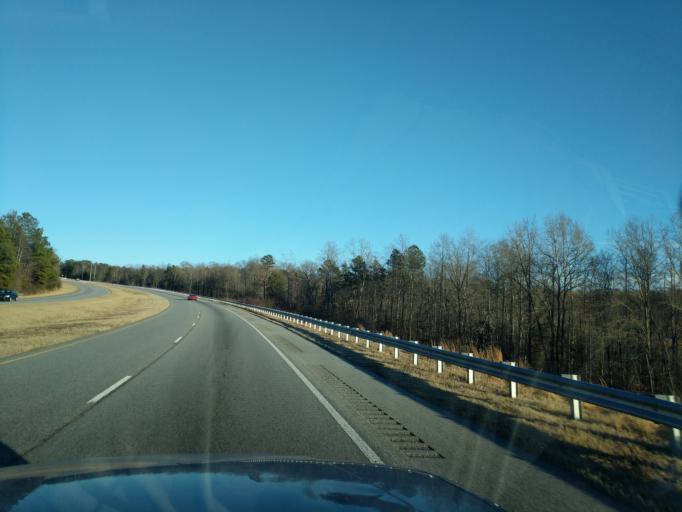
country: US
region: Georgia
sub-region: Stephens County
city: Toccoa
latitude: 34.5319
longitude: -83.3074
